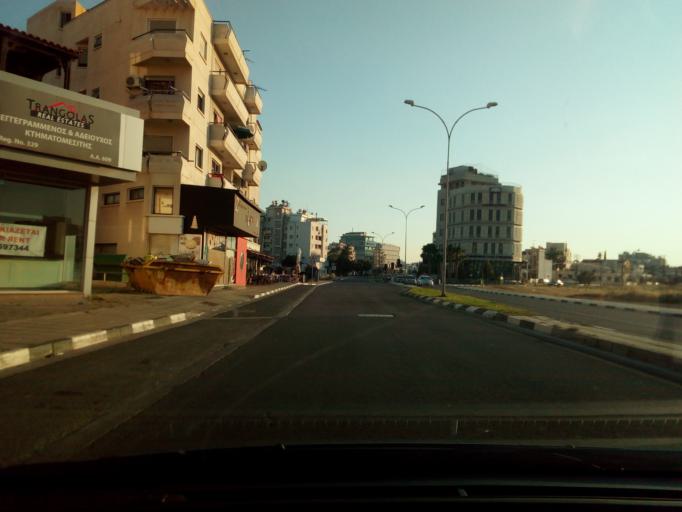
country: CY
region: Larnaka
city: Larnaca
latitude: 34.9200
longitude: 33.6159
